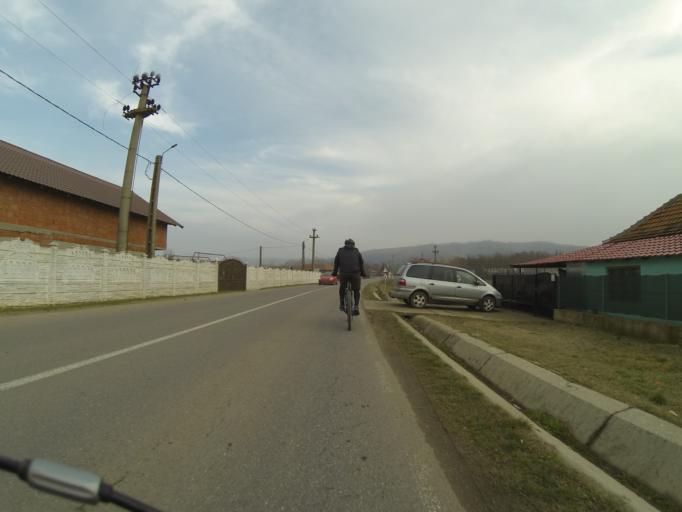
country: RO
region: Mehedinti
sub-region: Comuna Corlatel
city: Corlatel
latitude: 44.3981
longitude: 22.9252
